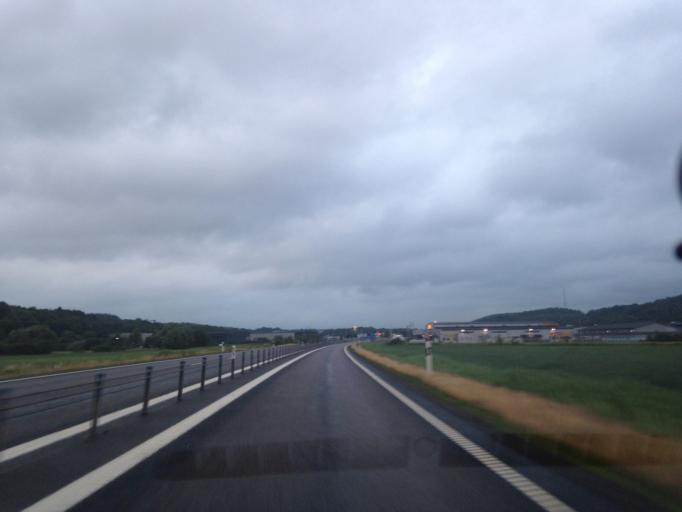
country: SE
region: Halland
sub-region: Varbergs Kommun
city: Varberg
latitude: 57.1611
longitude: 12.2728
